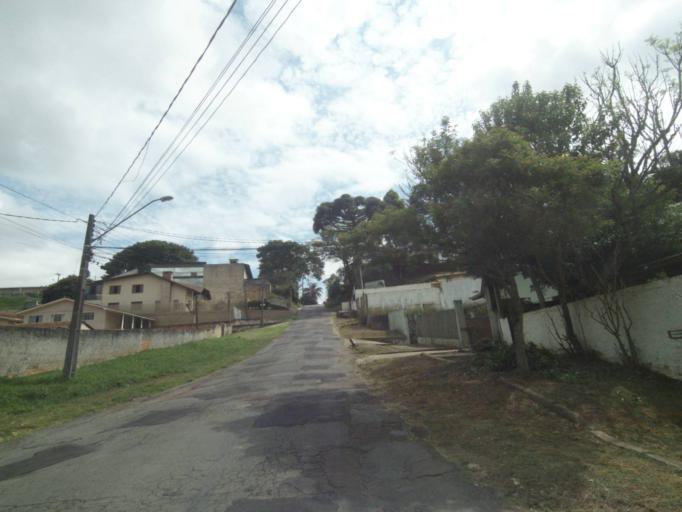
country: BR
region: Parana
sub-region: Curitiba
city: Curitiba
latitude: -25.3834
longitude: -49.2851
